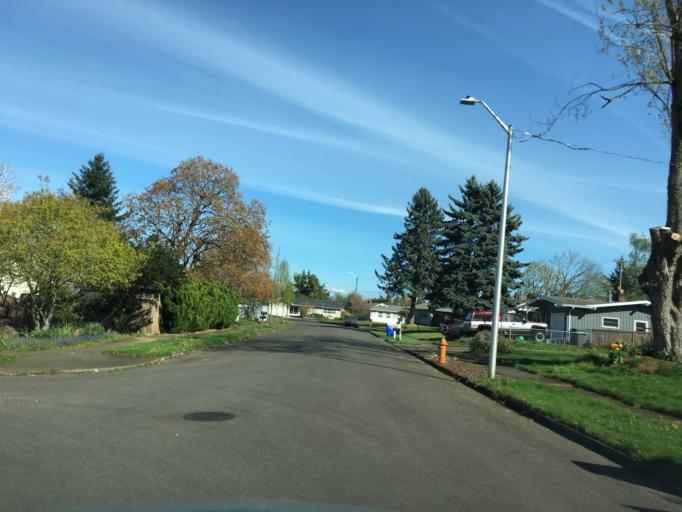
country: US
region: Oregon
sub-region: Multnomah County
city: Lents
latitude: 45.5415
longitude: -122.5216
